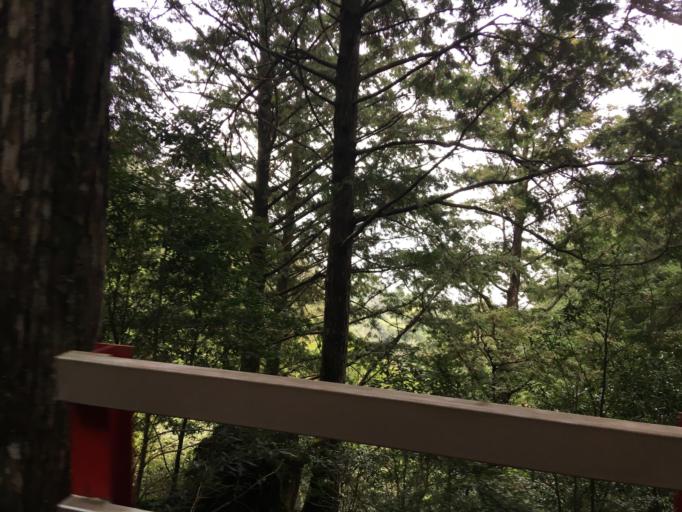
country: TW
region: Taiwan
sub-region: Yilan
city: Yilan
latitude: 24.4864
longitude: 121.5343
